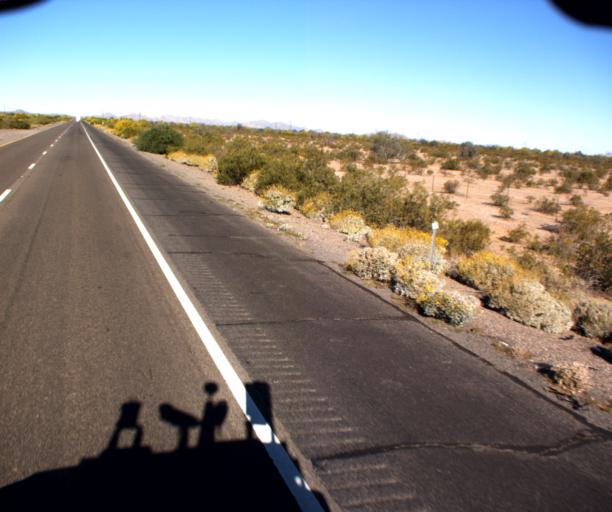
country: US
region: Arizona
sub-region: Pinal County
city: Casa Grande
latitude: 32.8292
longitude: -111.9879
